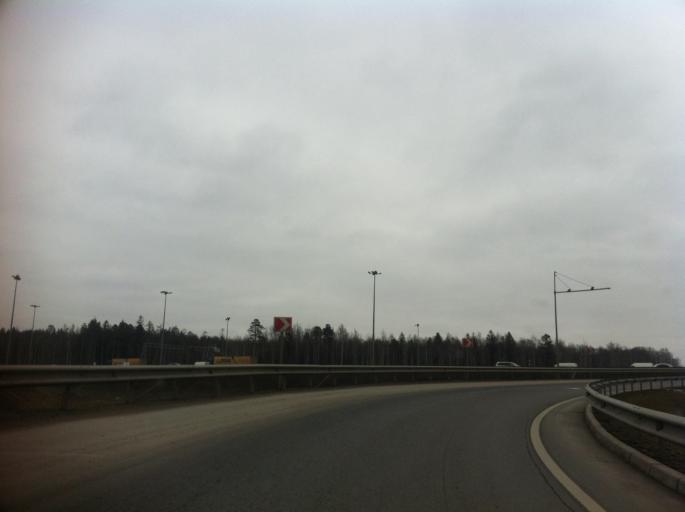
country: RU
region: St.-Petersburg
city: Krasnogvargeisky
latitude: 59.9474
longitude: 30.5396
